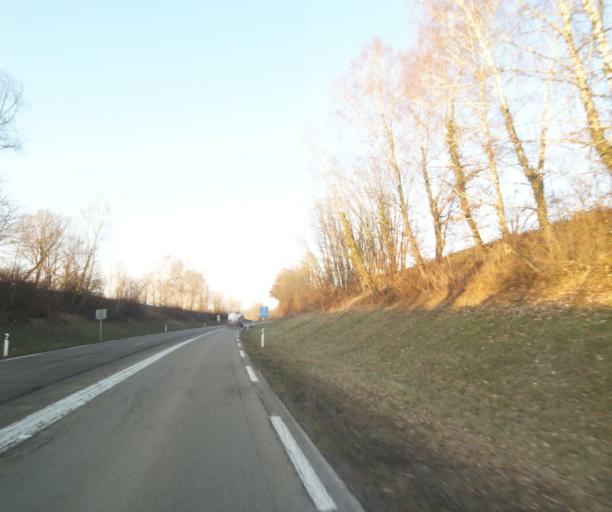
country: FR
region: Champagne-Ardenne
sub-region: Departement de la Haute-Marne
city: Bienville
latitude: 48.5832
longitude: 5.0284
